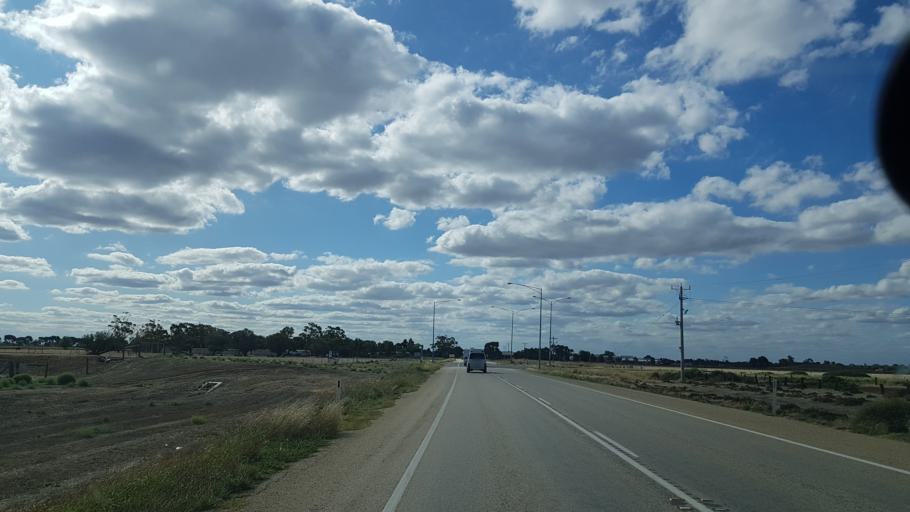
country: AU
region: Victoria
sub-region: Swan Hill
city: Swan Hill
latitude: -35.7642
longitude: 143.9316
